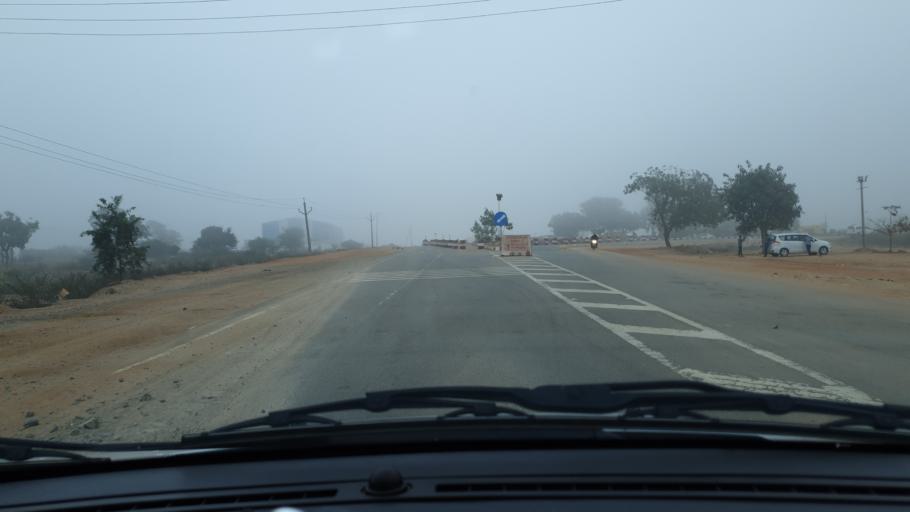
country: IN
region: Telangana
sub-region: Mahbubnagar
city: Nagar Karnul
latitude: 16.6616
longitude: 78.5758
